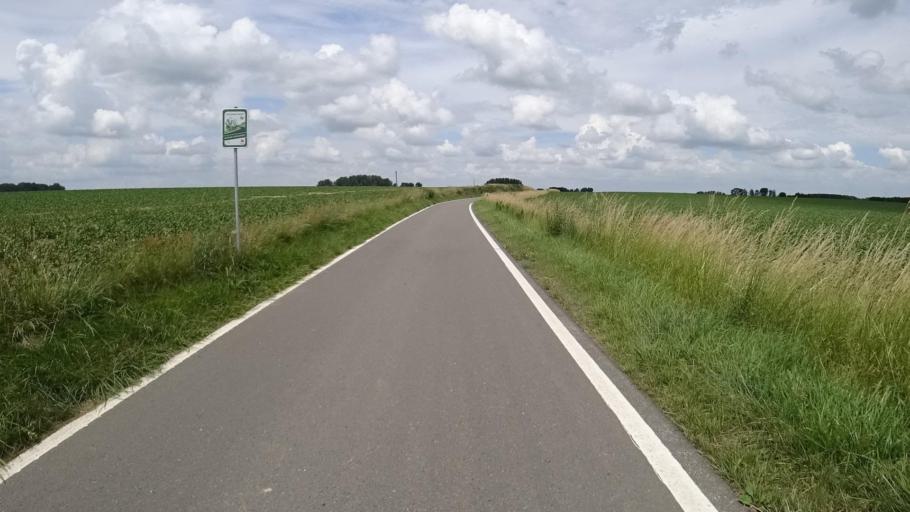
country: BE
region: Wallonia
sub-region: Province du Brabant Wallon
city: Perwez
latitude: 50.5519
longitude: 4.8323
